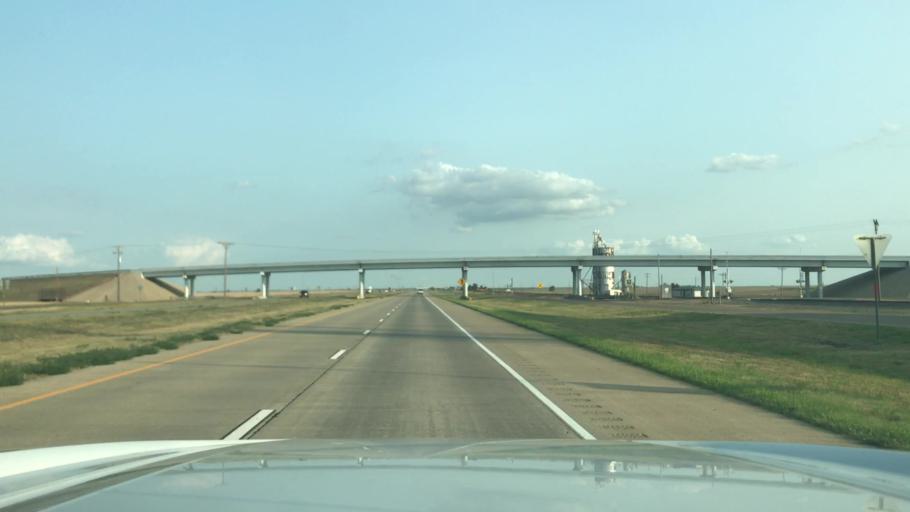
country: US
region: Texas
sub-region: Swisher County
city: Tulia
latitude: 34.6337
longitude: -101.8203
